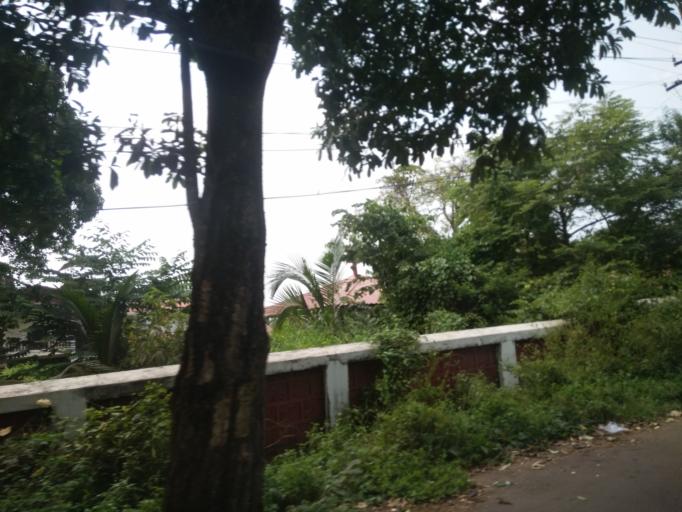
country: IN
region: Goa
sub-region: North Goa
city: Panaji
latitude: 15.5222
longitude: 73.8278
